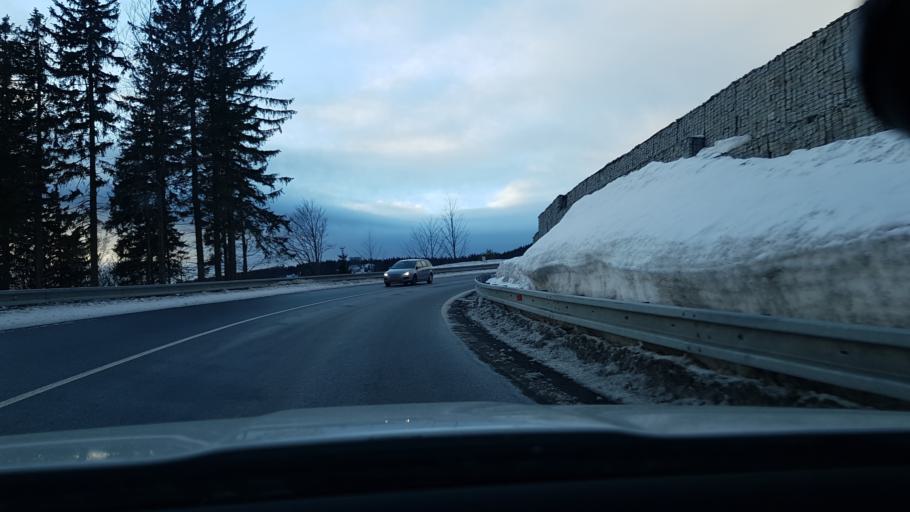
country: CZ
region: Olomoucky
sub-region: Okres Sumperk
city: Loucna nad Desnou
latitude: 50.1155
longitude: 17.1475
